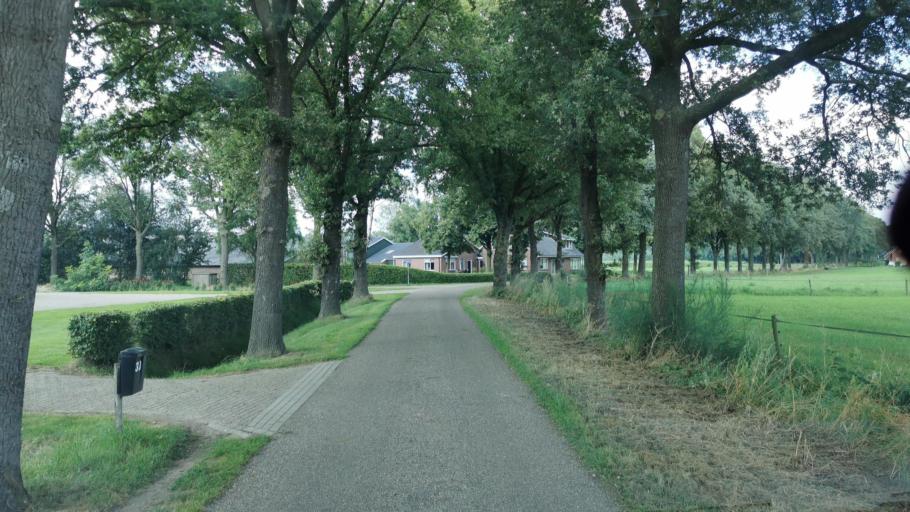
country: NL
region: Overijssel
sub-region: Gemeente Oldenzaal
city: Oldenzaal
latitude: 52.3366
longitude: 6.8537
